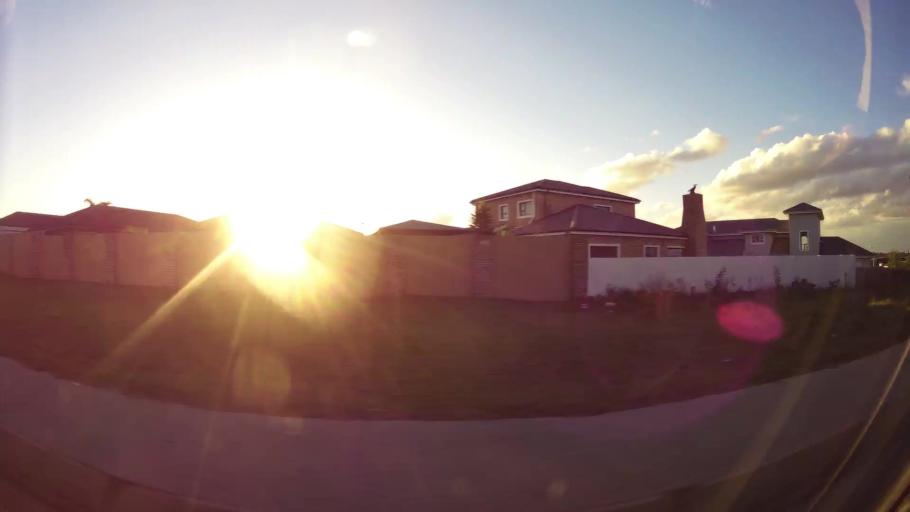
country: ZA
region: Eastern Cape
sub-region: Nelson Mandela Bay Metropolitan Municipality
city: Port Elizabeth
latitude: -33.9663
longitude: 25.5000
